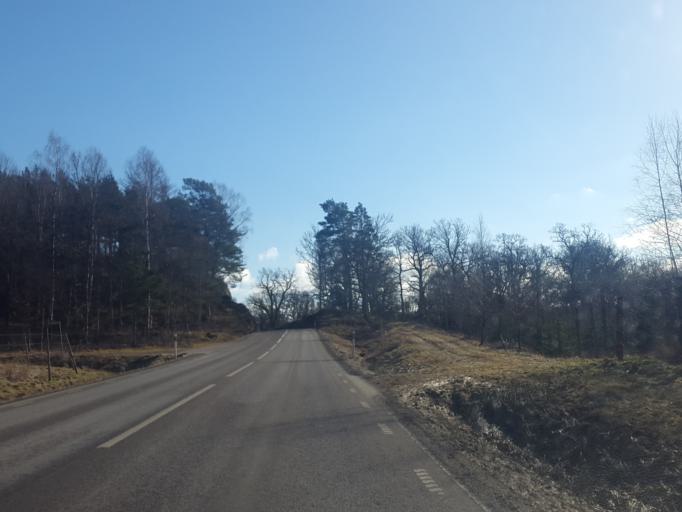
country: SE
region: Vaestra Goetaland
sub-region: Alingsas Kommun
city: Alingsas
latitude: 57.9586
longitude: 12.4503
